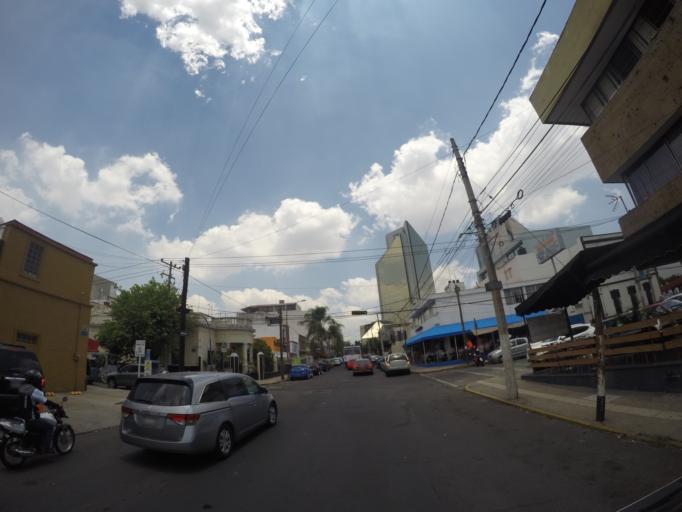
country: MX
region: Jalisco
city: Guadalajara
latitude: 20.6761
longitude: -103.3670
